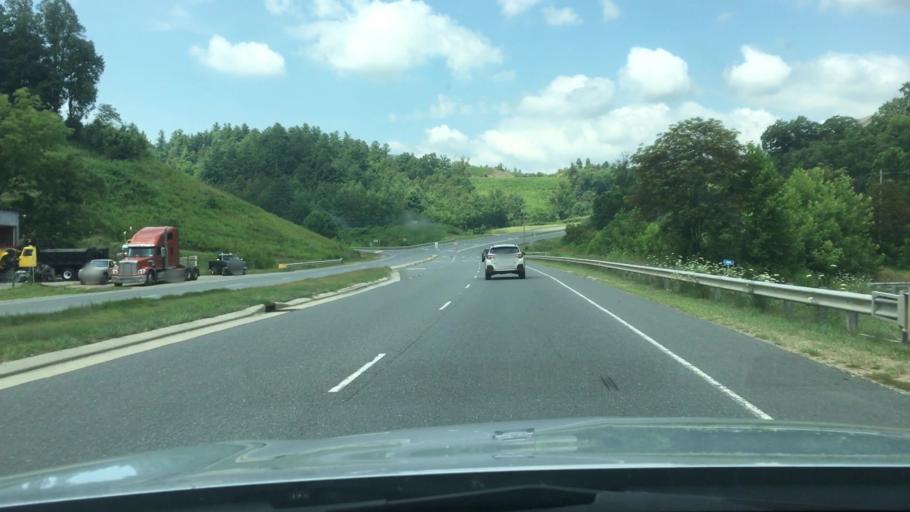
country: US
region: North Carolina
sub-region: Madison County
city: Mars Hill
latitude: 35.8408
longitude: -82.5071
